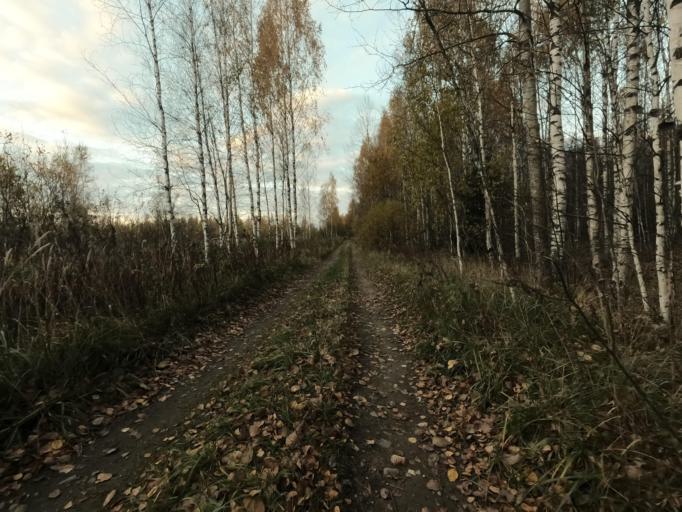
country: RU
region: Leningrad
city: Mga
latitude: 59.8213
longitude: 31.1780
